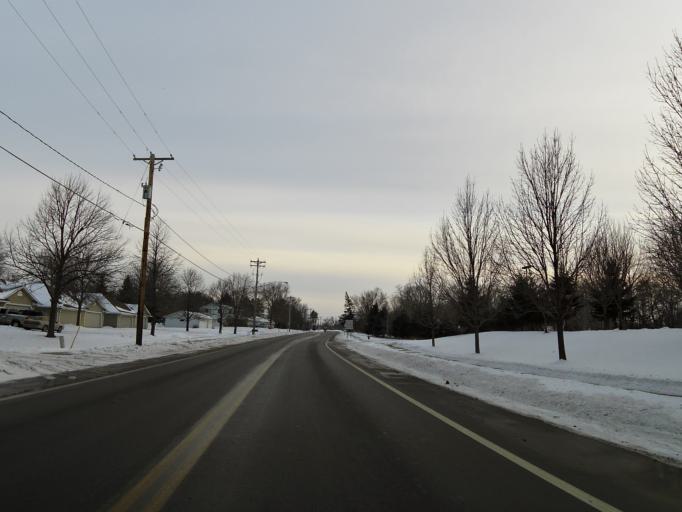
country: US
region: Minnesota
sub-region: Carver County
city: Victoria
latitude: 44.8545
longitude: -93.6606
